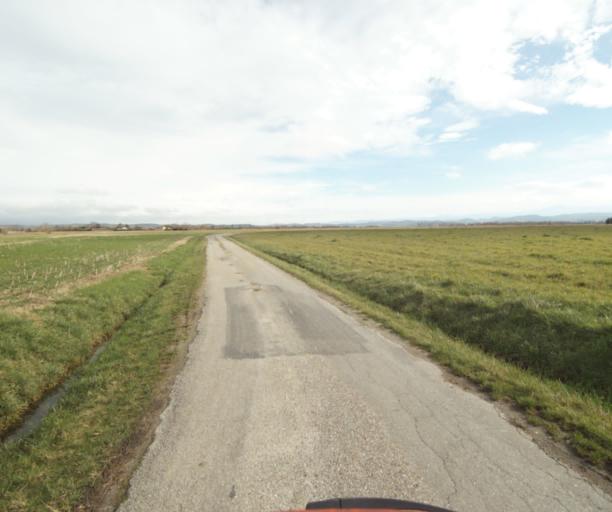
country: FR
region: Midi-Pyrenees
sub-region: Departement de l'Ariege
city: La Tour-du-Crieu
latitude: 43.1188
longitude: 1.7031
